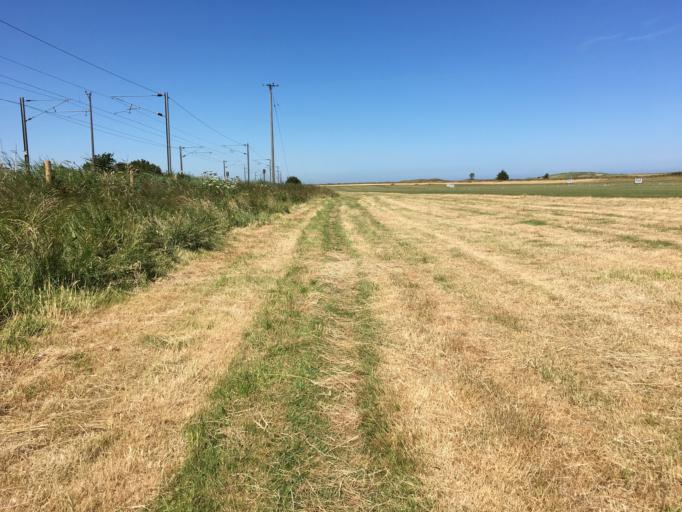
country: GB
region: England
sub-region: Northumberland
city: Ancroft
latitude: 55.7065
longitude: -1.9284
